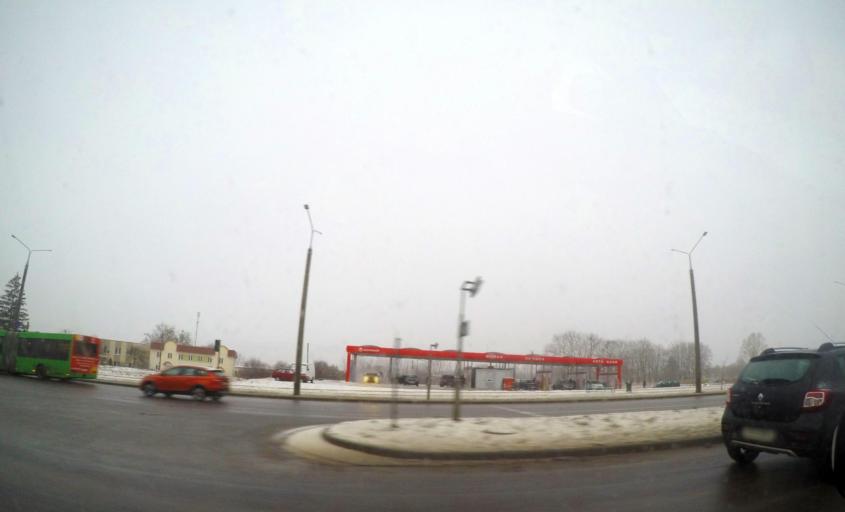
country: BY
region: Grodnenskaya
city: Hrodna
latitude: 53.6411
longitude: 23.8168
